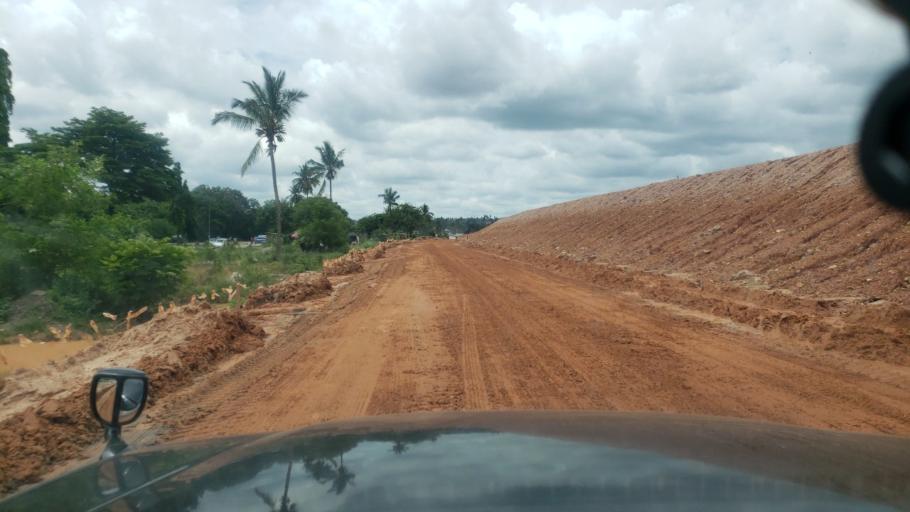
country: TZ
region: Pwani
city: Kisarawe
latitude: -6.8844
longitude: 39.1501
